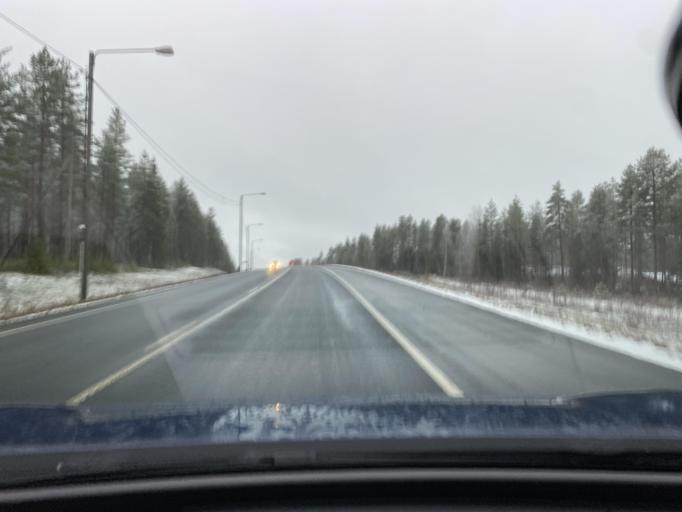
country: FI
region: Northern Ostrobothnia
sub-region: Oulu
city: Kiiminki
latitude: 65.1236
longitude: 25.7575
